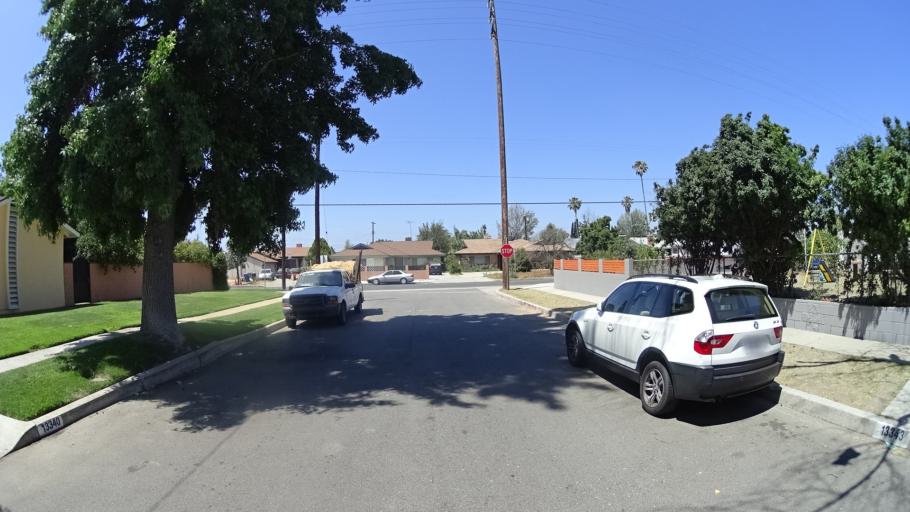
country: US
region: California
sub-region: Los Angeles County
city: San Fernando
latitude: 34.2356
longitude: -118.4246
